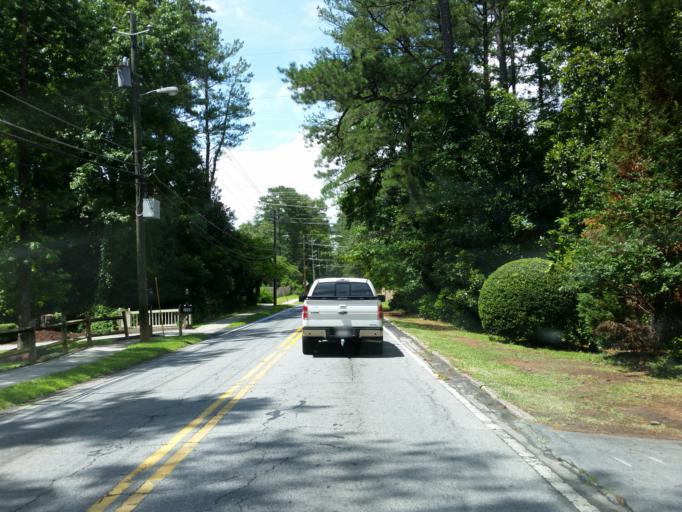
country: US
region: Georgia
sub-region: DeKalb County
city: Dunwoody
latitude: 33.9634
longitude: -84.3466
